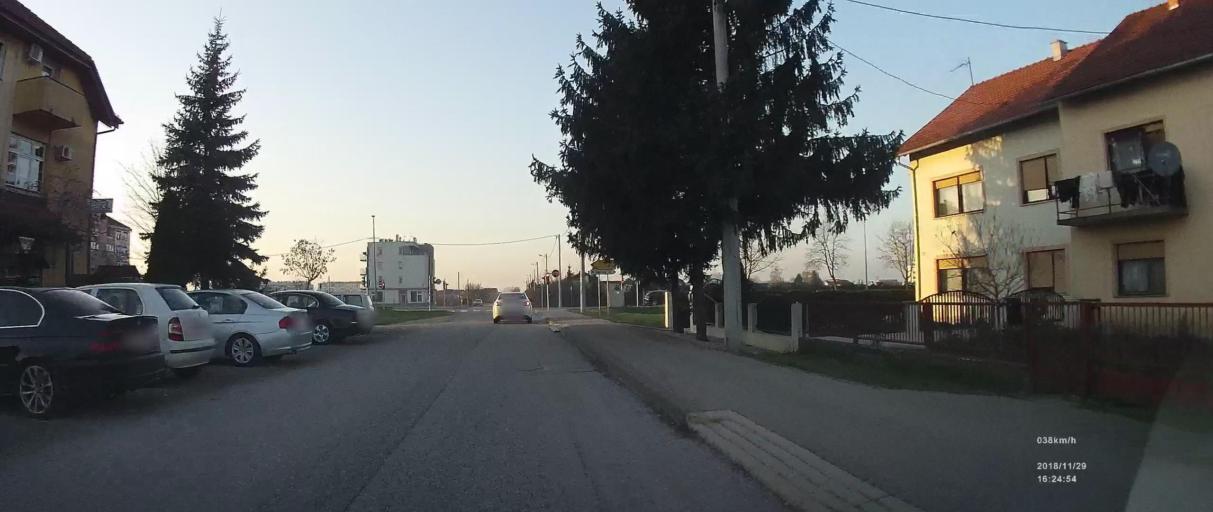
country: HR
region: Zagrebacka
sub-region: Grad Velika Gorica
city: Velika Gorica
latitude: 45.7053
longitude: 16.0649
